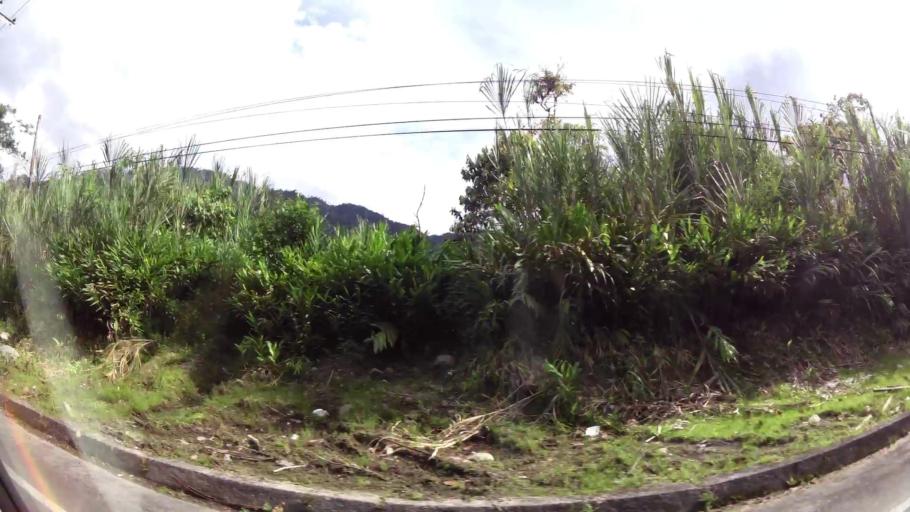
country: EC
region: Pastaza
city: Puyo
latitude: -1.4125
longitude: -78.2029
